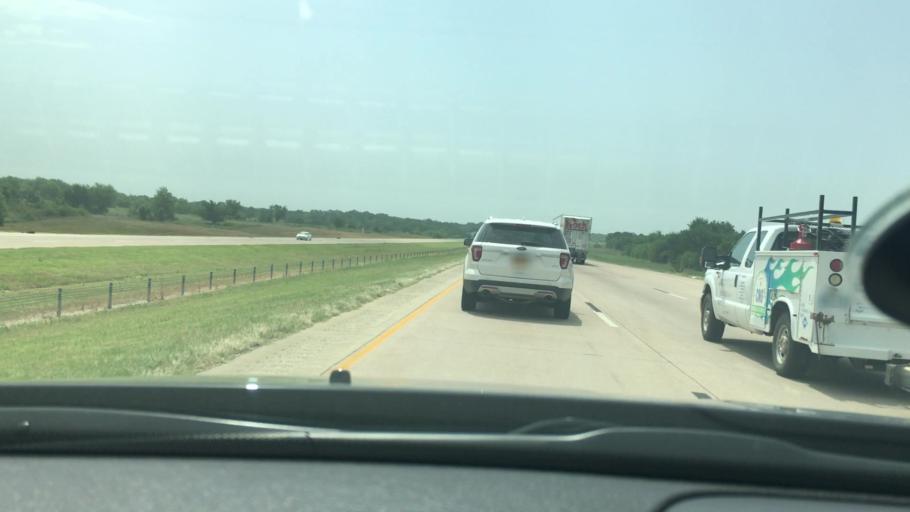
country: US
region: Oklahoma
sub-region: Garvin County
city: Pauls Valley
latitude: 34.7018
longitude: -97.2416
